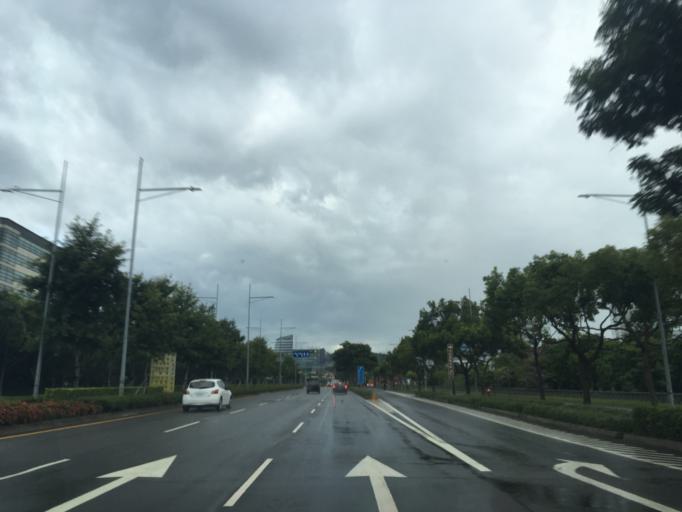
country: TW
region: Taiwan
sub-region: Taichung City
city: Taichung
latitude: 24.2076
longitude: 120.6220
